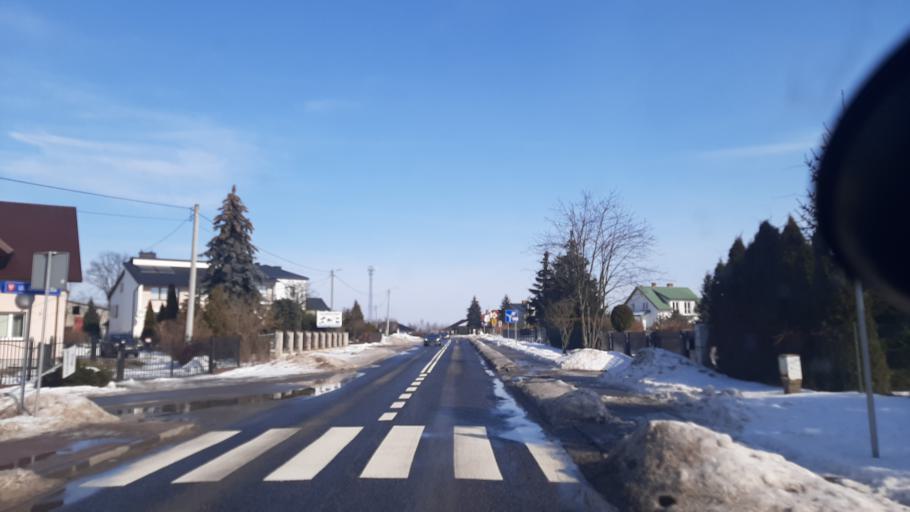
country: PL
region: Lublin Voivodeship
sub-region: Powiat pulawski
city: Kurow
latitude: 51.3954
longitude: 22.1961
